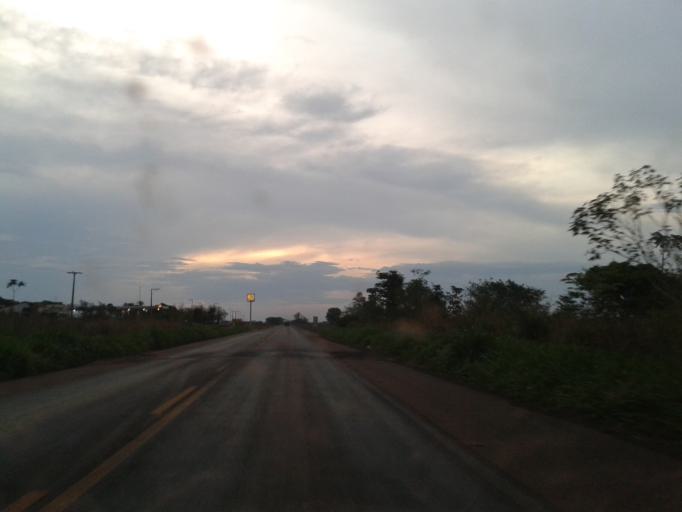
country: BR
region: Goias
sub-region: Santa Helena De Goias
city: Santa Helena de Goias
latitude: -17.8780
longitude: -50.7096
